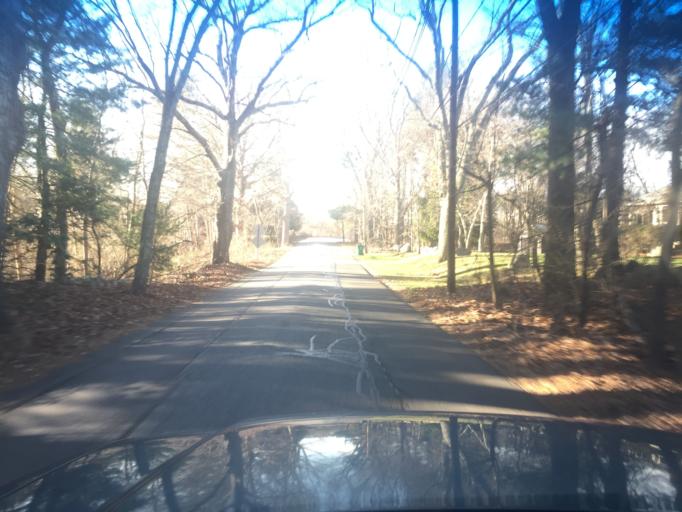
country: US
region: Massachusetts
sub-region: Middlesex County
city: Hopkinton
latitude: 42.2311
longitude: -71.4857
